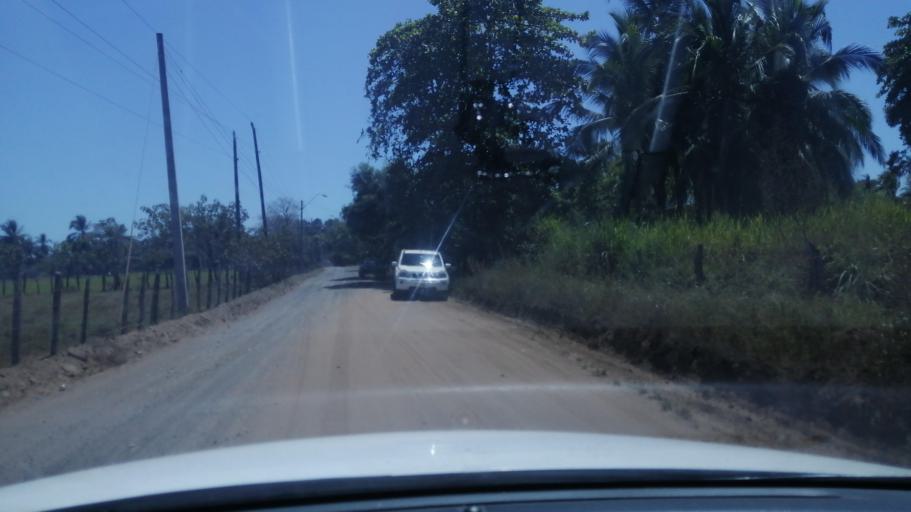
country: PA
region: Chiriqui
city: San Felix
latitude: 8.1700
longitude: -81.8669
